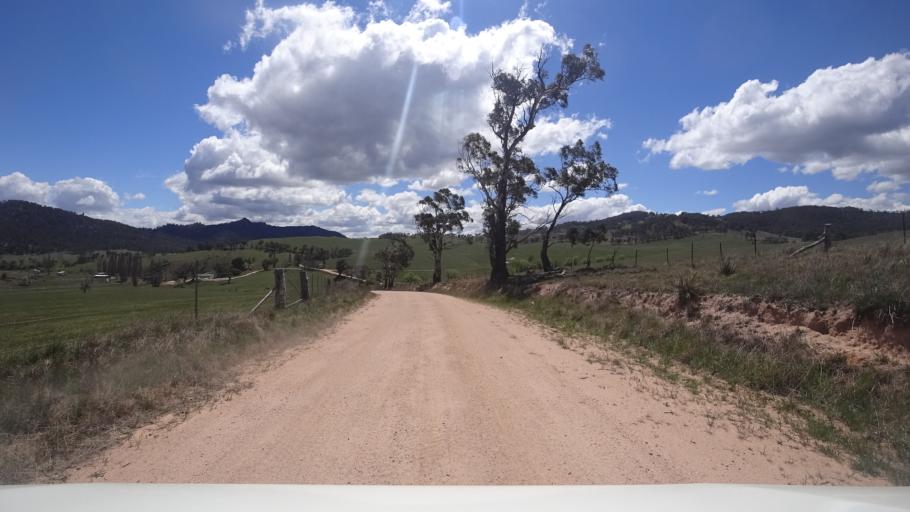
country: AU
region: New South Wales
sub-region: Oberon
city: Oberon
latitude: -33.5686
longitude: 149.9423
